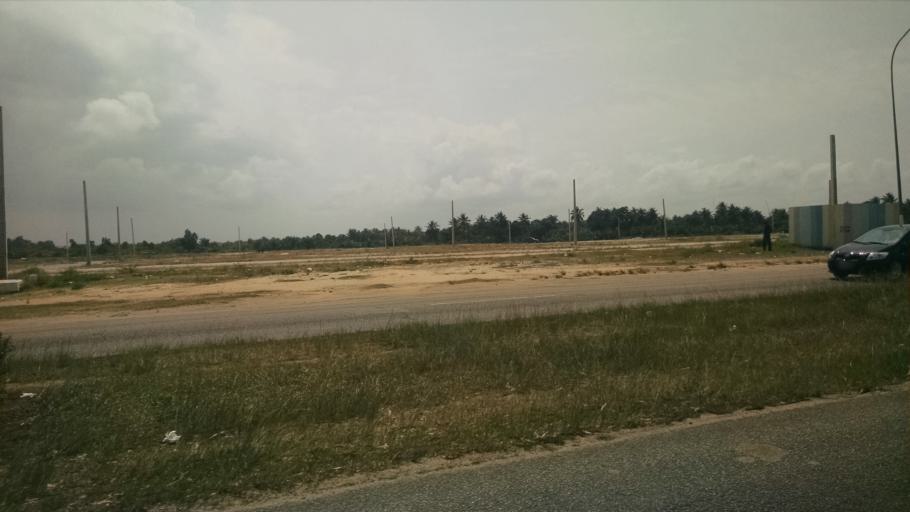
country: CI
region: Lagunes
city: Abidjan
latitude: 5.2622
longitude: -3.9472
